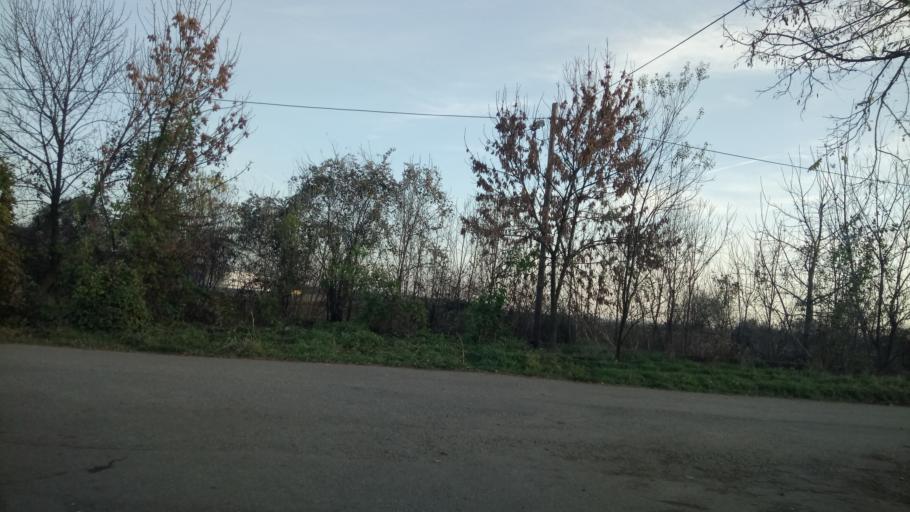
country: RS
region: Autonomna Pokrajina Vojvodina
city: Nova Pazova
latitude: 44.9353
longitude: 20.2262
